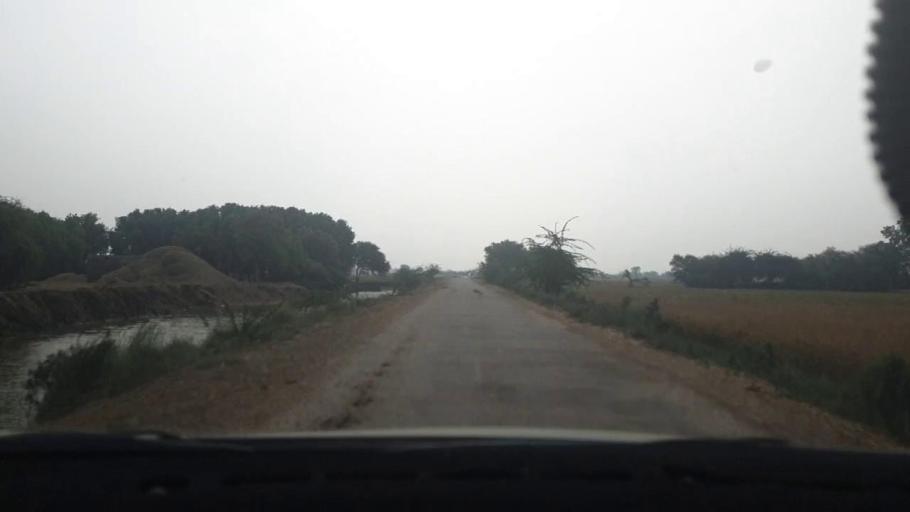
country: PK
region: Sindh
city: Tando Muhammad Khan
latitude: 25.0590
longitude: 68.5452
